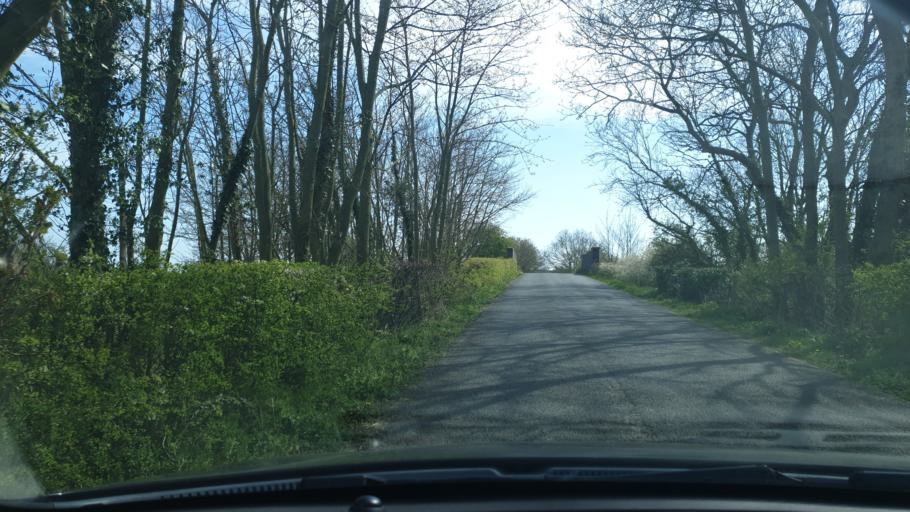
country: GB
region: England
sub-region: Essex
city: Great Bentley
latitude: 51.8533
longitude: 1.0862
